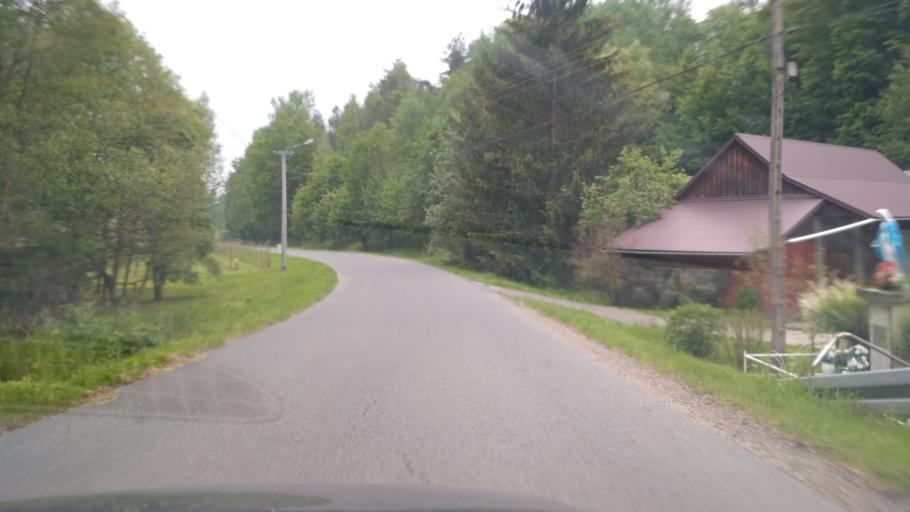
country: PL
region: Subcarpathian Voivodeship
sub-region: Powiat ropczycko-sedziszowski
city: Zagorzyce
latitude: 49.9948
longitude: 21.6929
